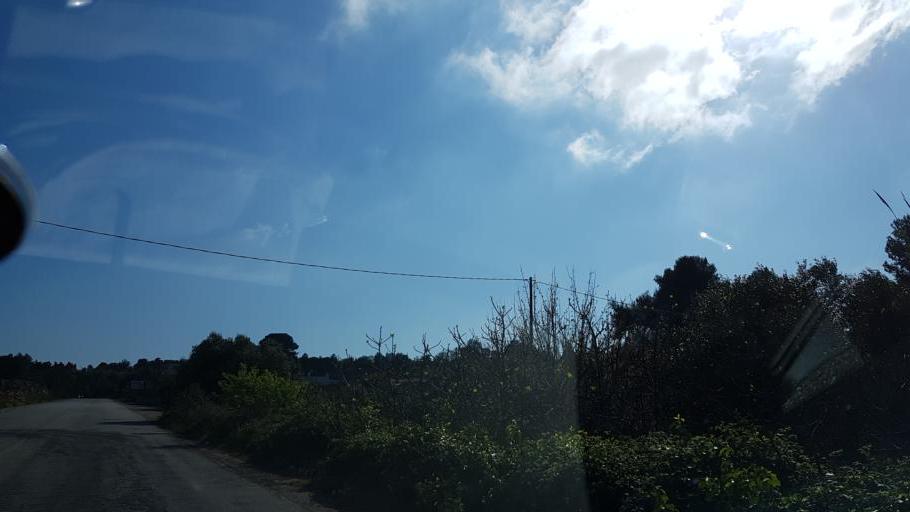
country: IT
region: Apulia
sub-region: Provincia di Brindisi
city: Ostuni
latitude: 40.7302
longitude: 17.5900
